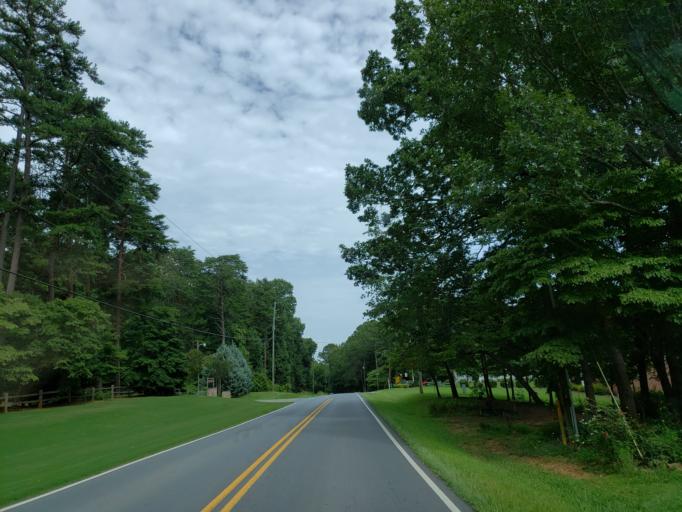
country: US
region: Georgia
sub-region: Pickens County
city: Jasper
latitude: 34.4465
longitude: -84.4172
